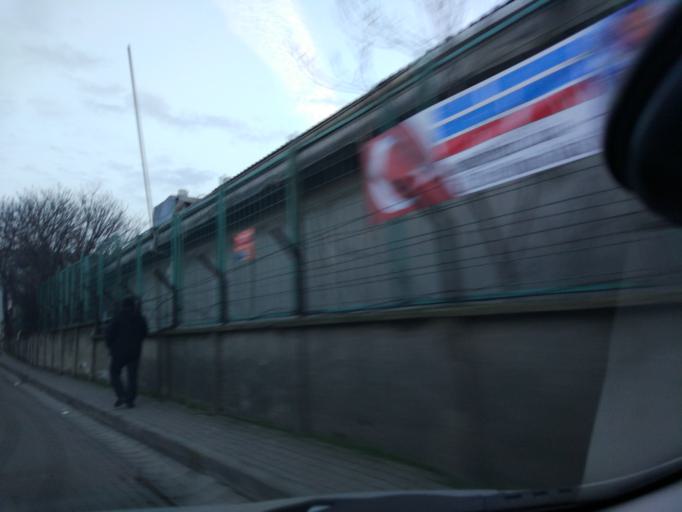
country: TR
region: Istanbul
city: Bahcelievler
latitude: 41.0104
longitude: 28.8244
